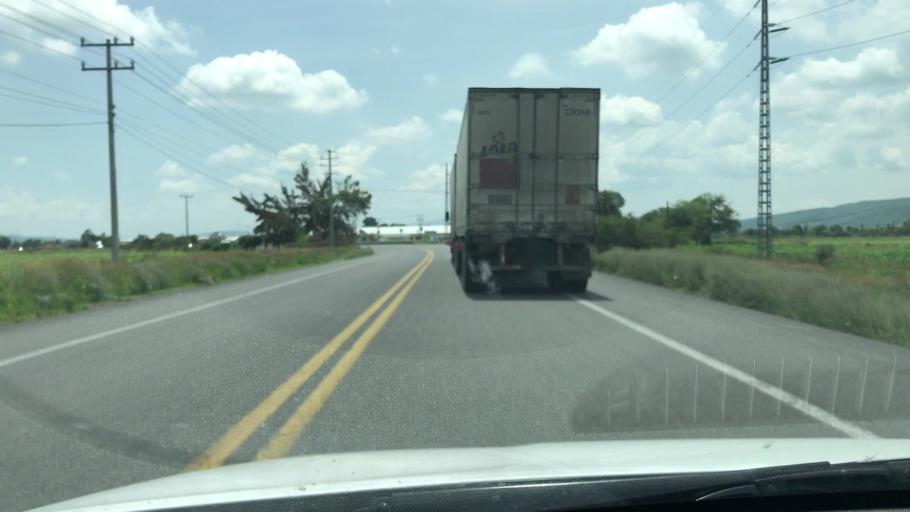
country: MX
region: Michoacan
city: Tanhuato de Guerrero
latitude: 20.2824
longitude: -102.3453
